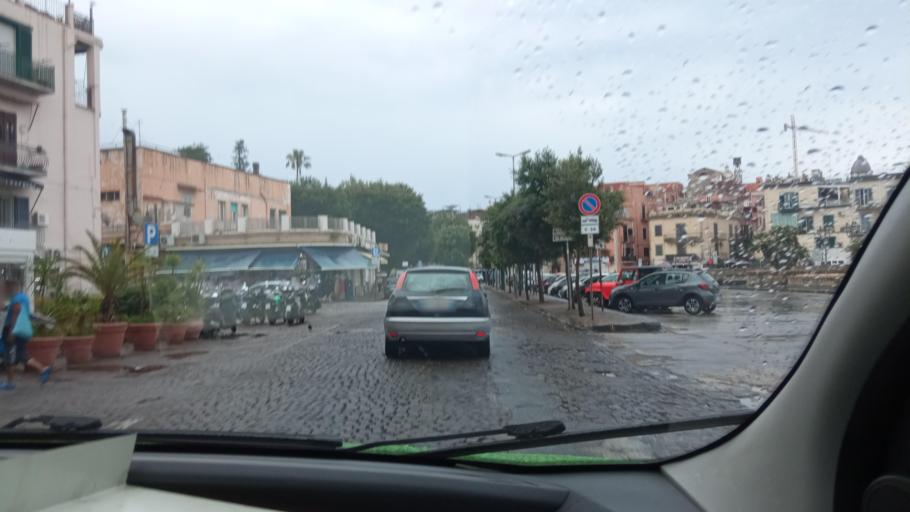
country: IT
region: Campania
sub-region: Provincia di Napoli
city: Pozzuoli
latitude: 40.8250
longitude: 14.1203
